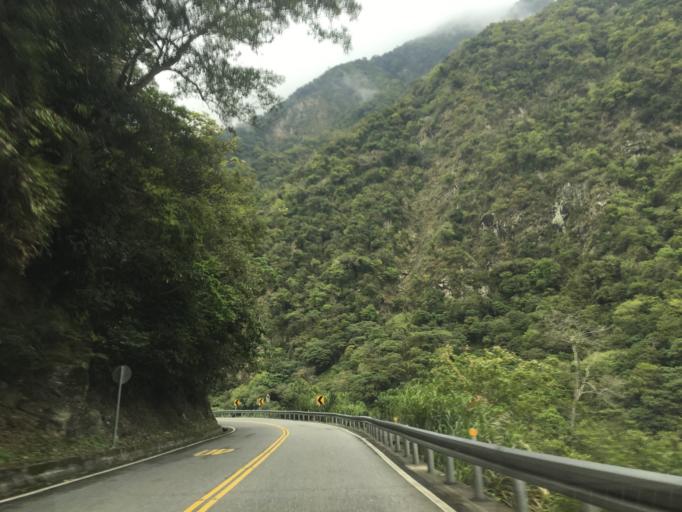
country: TW
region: Taiwan
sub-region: Hualien
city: Hualian
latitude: 24.1762
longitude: 121.5873
